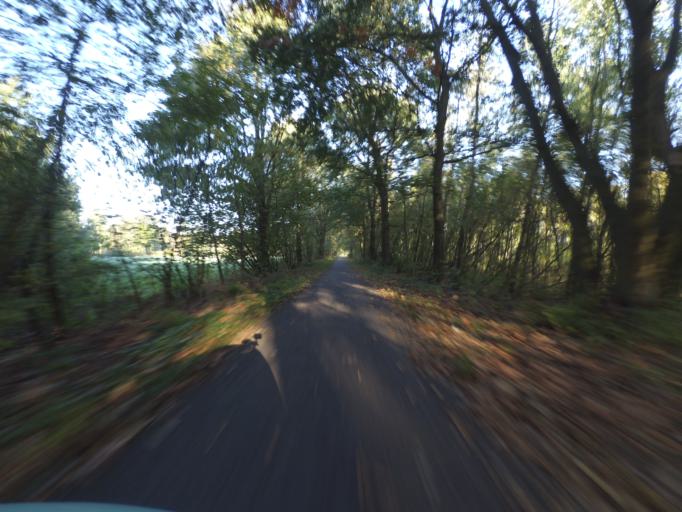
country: NL
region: Gelderland
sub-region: Gemeente Winterswijk
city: Winterswijk
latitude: 51.9954
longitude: 6.6697
